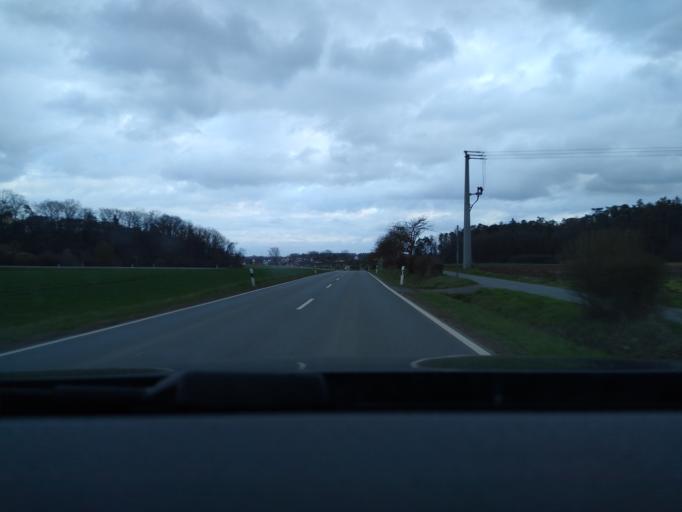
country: DE
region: Bavaria
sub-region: Regierungsbezirk Mittelfranken
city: Zirndorf
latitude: 49.4552
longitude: 10.9177
